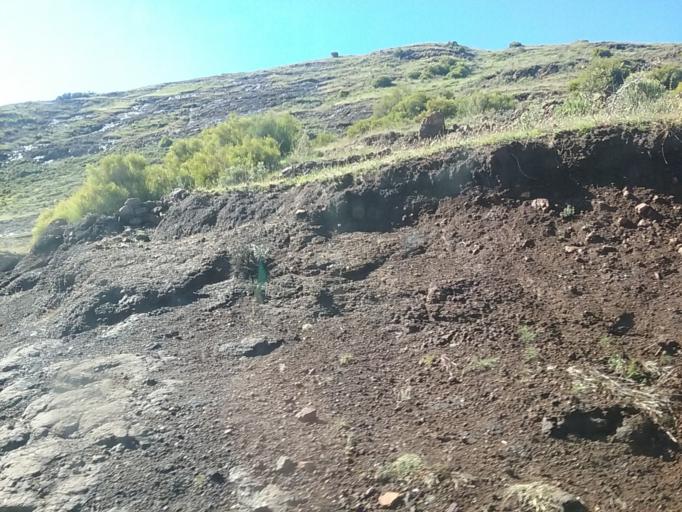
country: LS
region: Berea
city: Teyateyaneng
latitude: -29.2343
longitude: 27.9196
